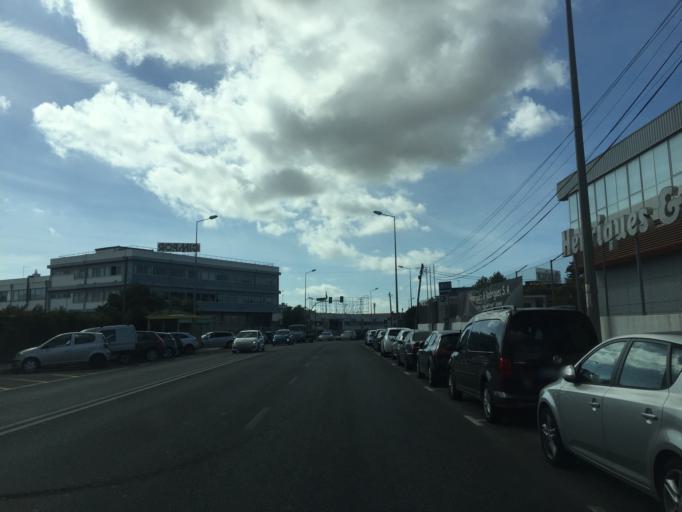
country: PT
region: Lisbon
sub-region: Loures
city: Sacavem
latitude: 38.7870
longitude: -9.1238
